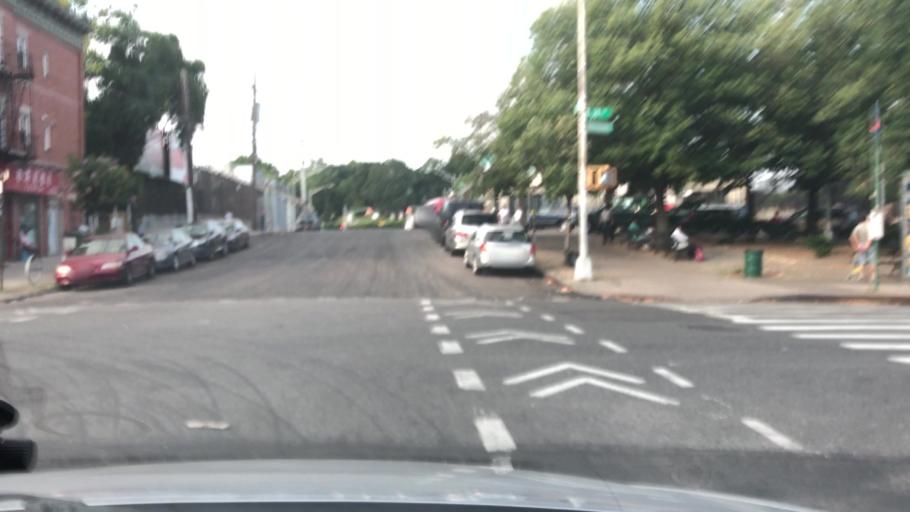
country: US
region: New York
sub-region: Kings County
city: Bensonhurst
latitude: 40.6458
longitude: -73.9952
